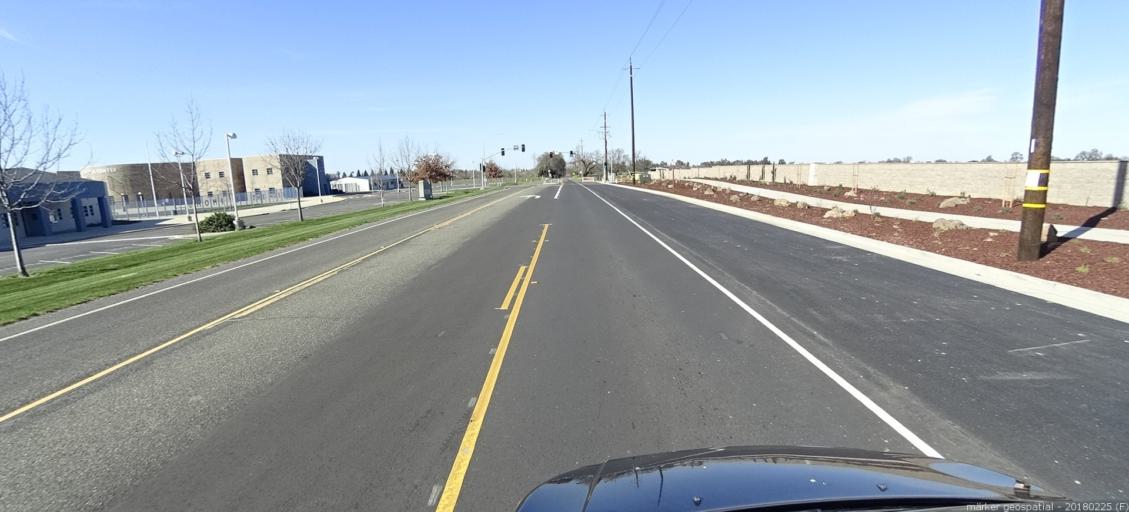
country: US
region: California
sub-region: Sacramento County
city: Antelope
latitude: 38.7288
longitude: -121.3674
